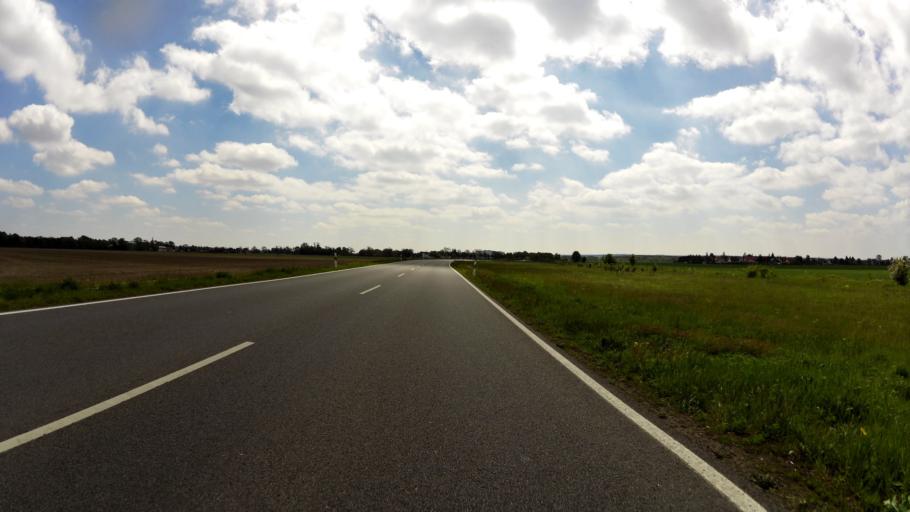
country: DE
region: Saxony
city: Torgau
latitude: 51.5202
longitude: 13.0325
